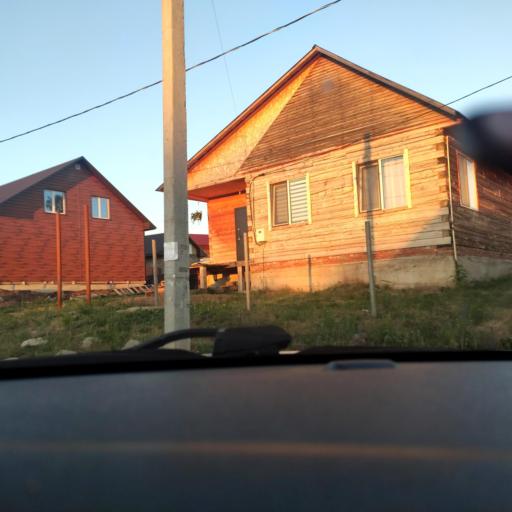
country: RU
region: Bashkortostan
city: Avdon
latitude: 54.6301
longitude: 55.6042
